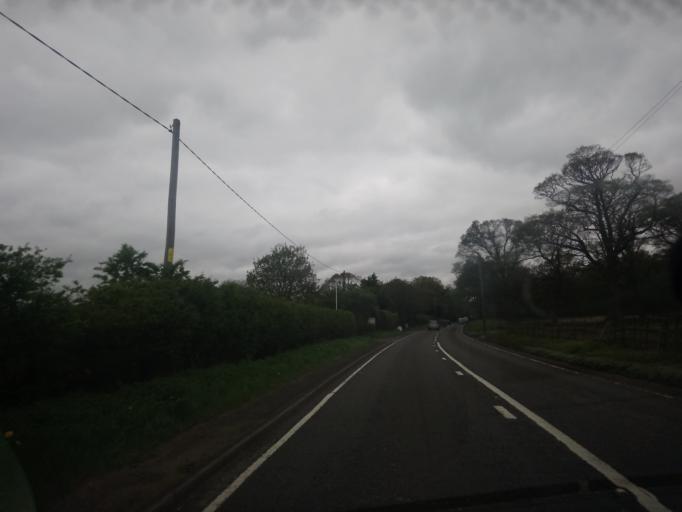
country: GB
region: England
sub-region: Telford and Wrekin
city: Chetwynd
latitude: 52.7949
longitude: -2.4148
